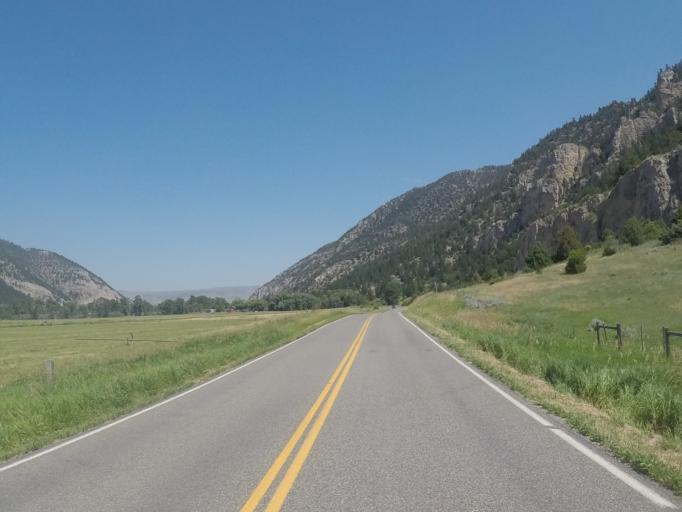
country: US
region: Montana
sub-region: Park County
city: Livingston
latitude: 45.5906
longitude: -110.5611
